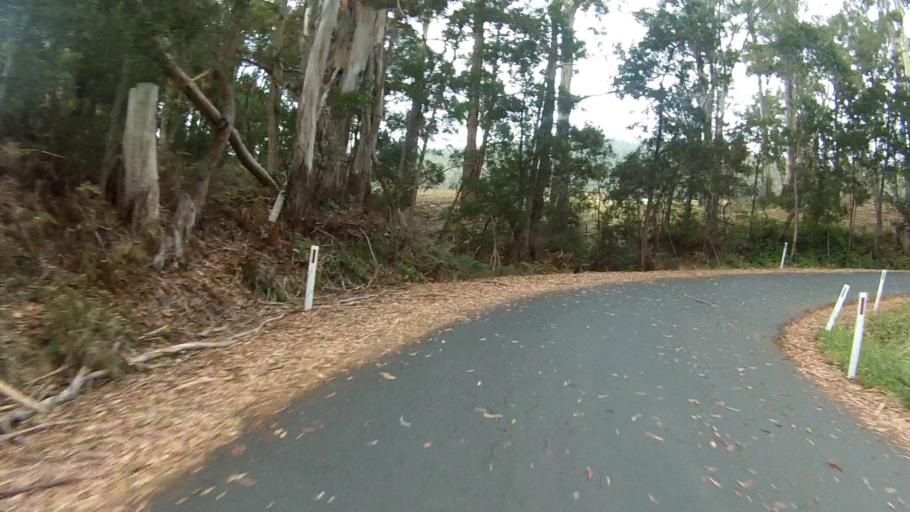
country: AU
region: Tasmania
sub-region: Huon Valley
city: Cygnet
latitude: -43.2158
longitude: 147.1120
